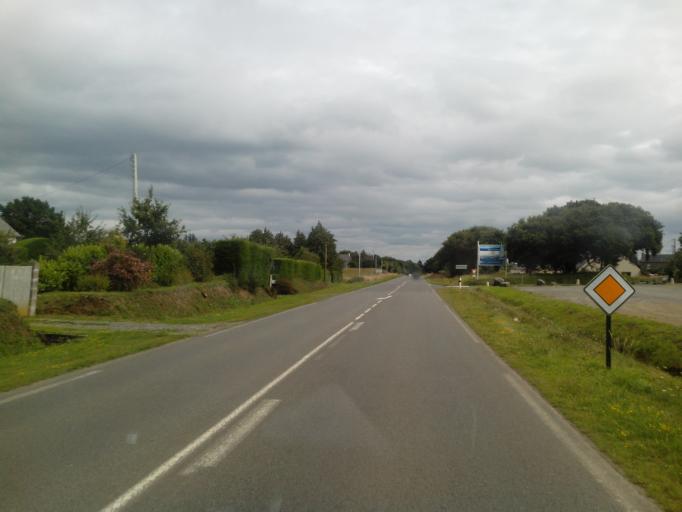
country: FR
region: Brittany
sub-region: Departement des Cotes-d'Armor
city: Saint-Quay-Portrieux
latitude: 48.6578
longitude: -2.8574
